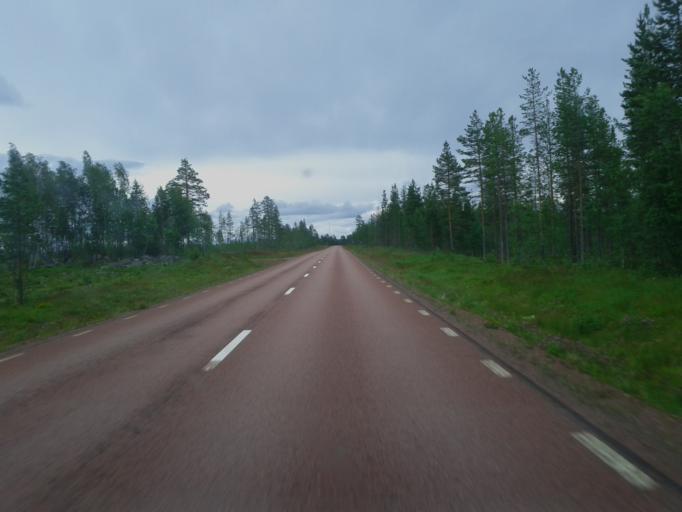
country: SE
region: Dalarna
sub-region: Alvdalens Kommun
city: AElvdalen
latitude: 61.5531
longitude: 13.3234
